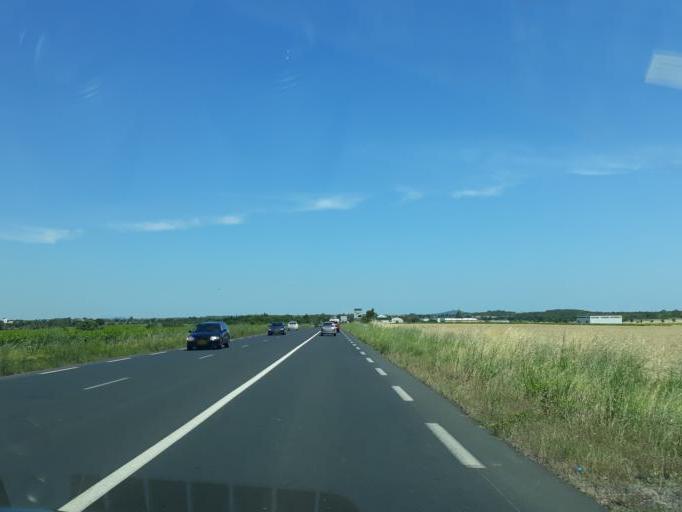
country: FR
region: Languedoc-Roussillon
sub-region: Departement de l'Herault
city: Portiragnes
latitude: 43.3131
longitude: 3.3314
